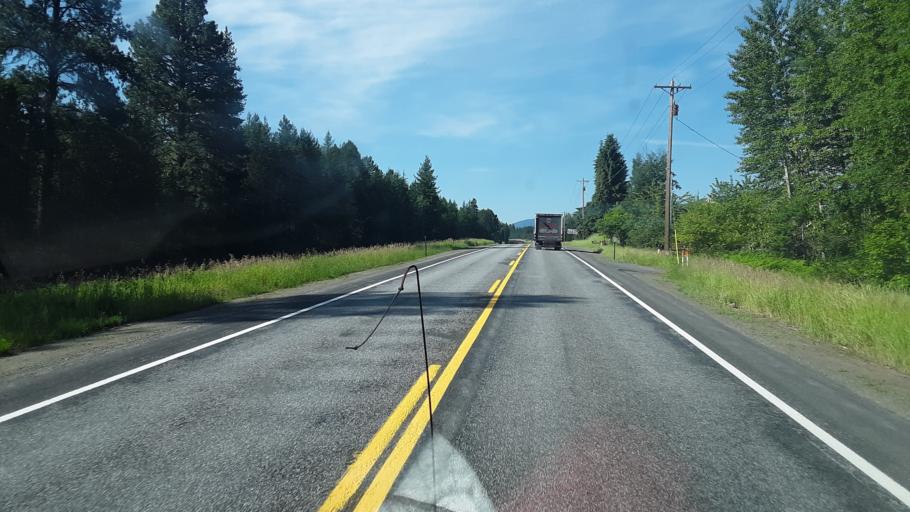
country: US
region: Idaho
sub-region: Bonner County
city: Ponderay
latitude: 48.4982
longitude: -116.4510
